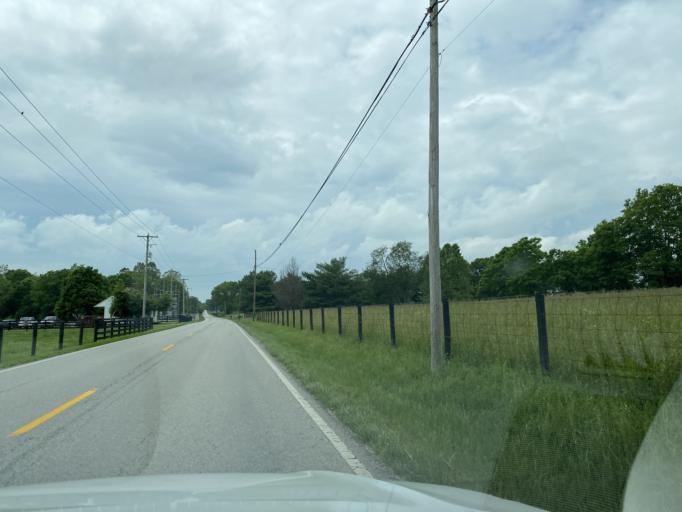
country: US
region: Kentucky
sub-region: Scott County
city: Georgetown
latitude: 38.2219
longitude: -84.4564
